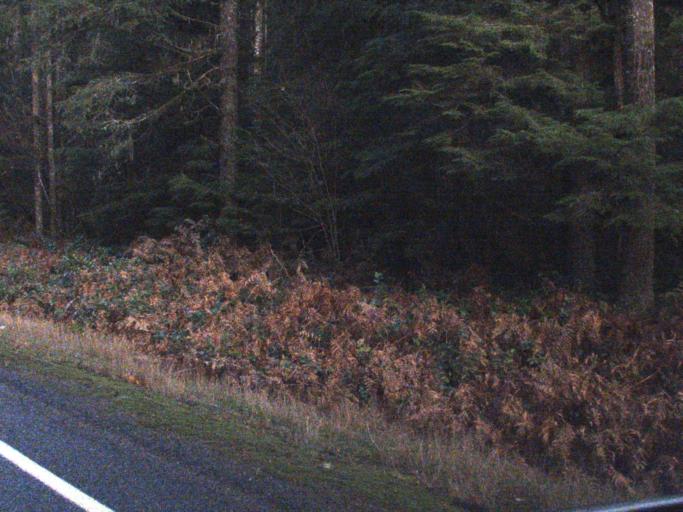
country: US
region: Washington
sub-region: Snohomish County
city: Darrington
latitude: 48.3551
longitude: -121.5399
